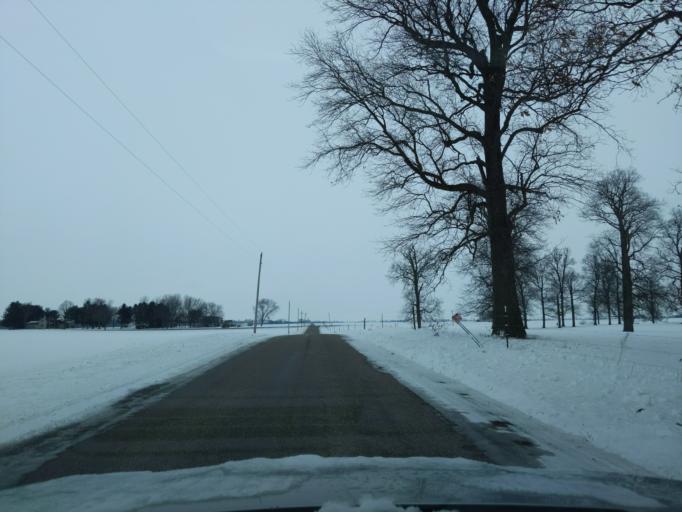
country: US
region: Indiana
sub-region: Benton County
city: Otterbein
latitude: 40.4432
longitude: -87.0928
